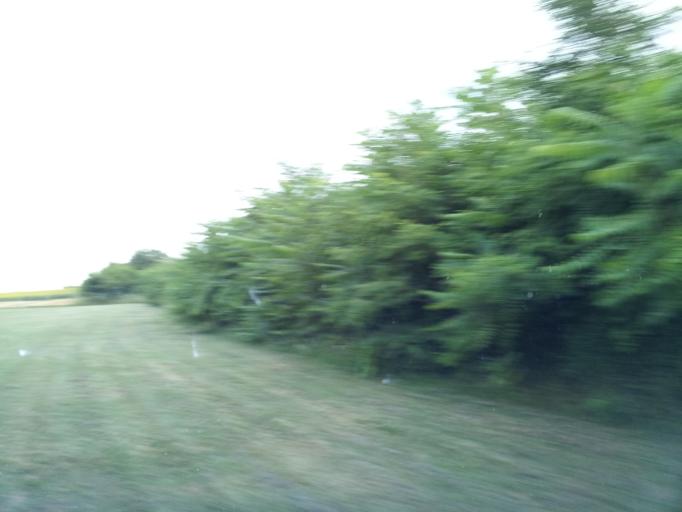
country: HU
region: Somogy
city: Adand
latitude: 46.8848
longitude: 18.1626
